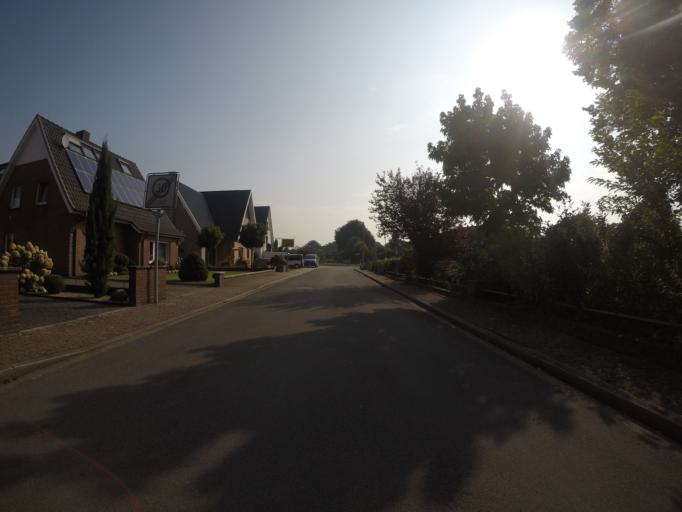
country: DE
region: North Rhine-Westphalia
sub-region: Regierungsbezirk Dusseldorf
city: Bocholt
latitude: 51.8336
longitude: 6.5502
